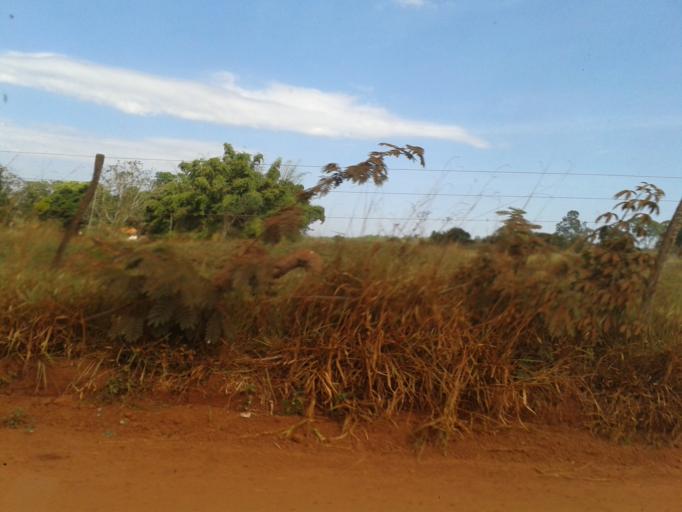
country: BR
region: Minas Gerais
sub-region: Ituiutaba
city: Ituiutaba
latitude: -19.0392
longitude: -49.3810
